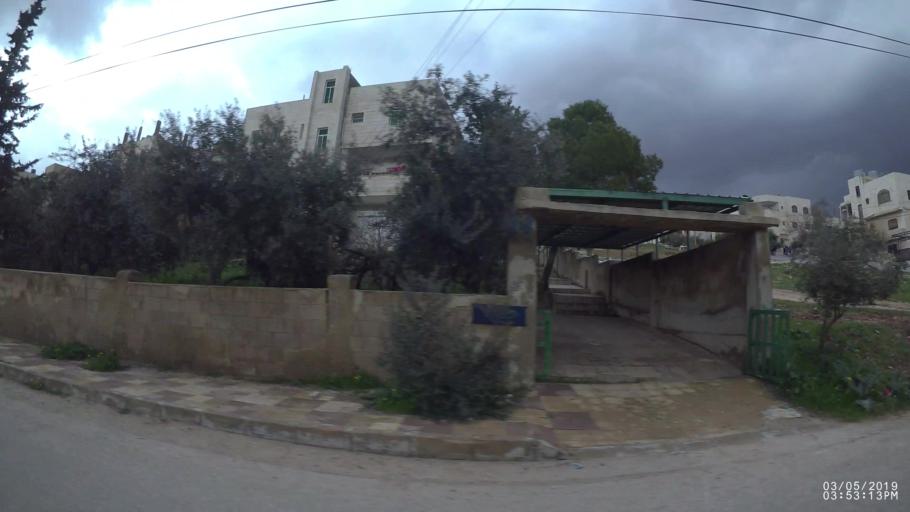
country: JO
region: Amman
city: Amman
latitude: 32.0089
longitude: 35.9465
